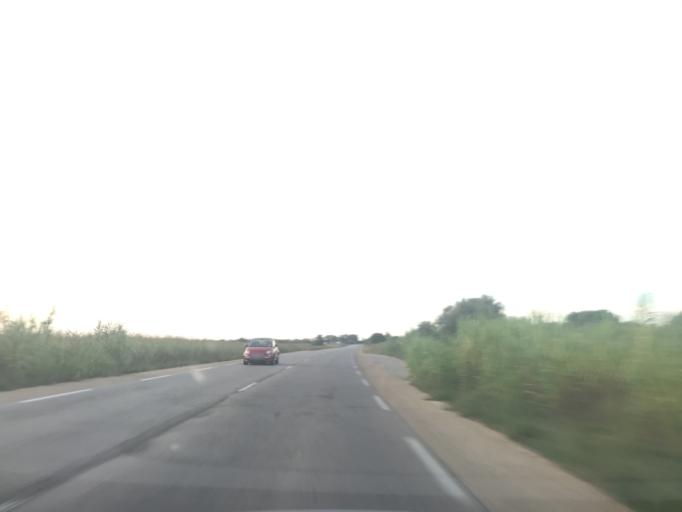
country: FR
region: Provence-Alpes-Cote d'Azur
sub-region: Departement des Bouches-du-Rhone
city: Saintes-Maries-de-la-Mer
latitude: 43.5113
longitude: 4.3986
